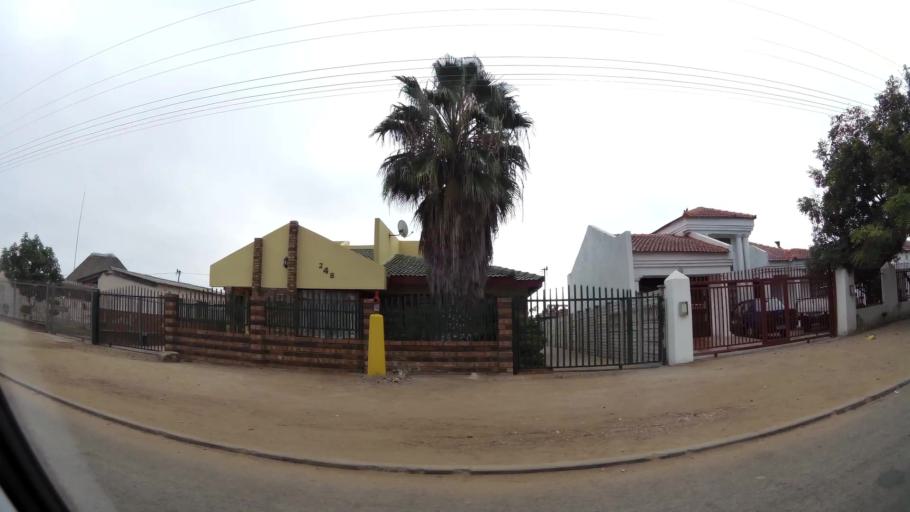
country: ZA
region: Limpopo
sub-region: Capricorn District Municipality
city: Polokwane
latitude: -23.8364
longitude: 29.3840
